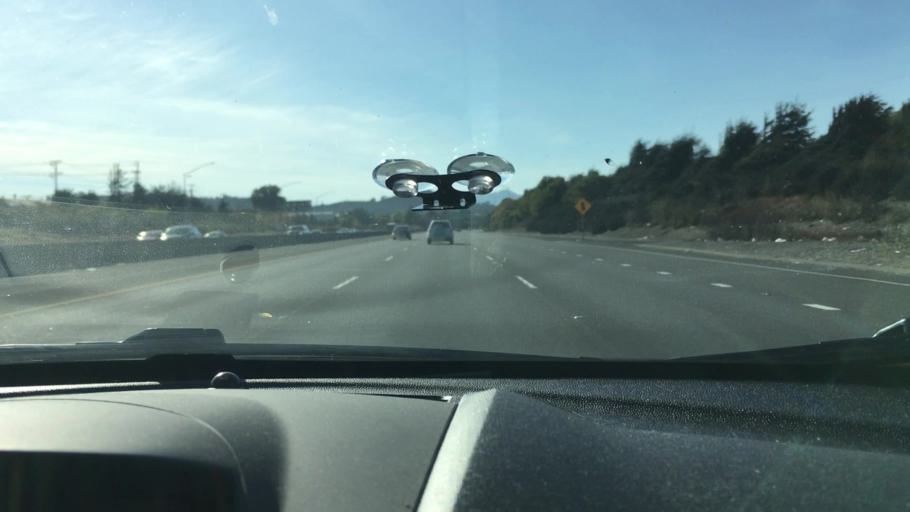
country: US
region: California
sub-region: Contra Costa County
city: Richmond
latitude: 37.9219
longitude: -122.3495
